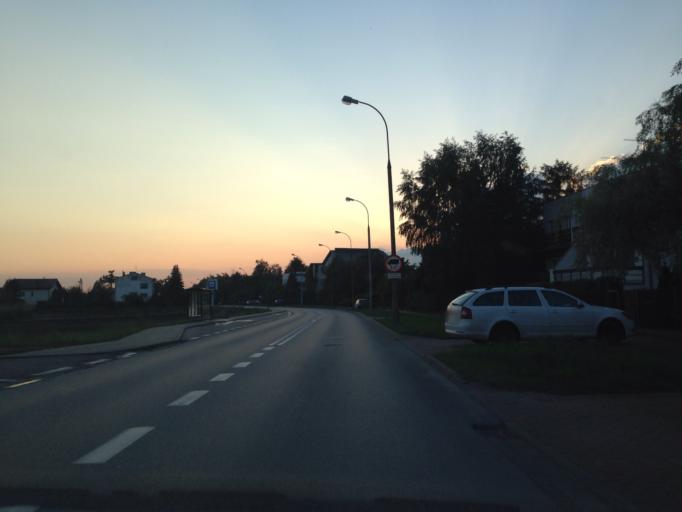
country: PL
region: Masovian Voivodeship
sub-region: Powiat warszawski zachodni
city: Babice
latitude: 52.2491
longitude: 20.8739
